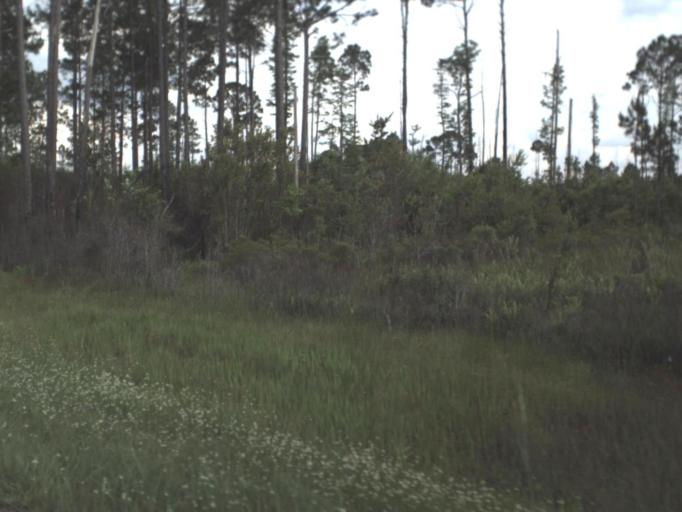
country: US
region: Florida
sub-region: Baker County
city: Macclenny
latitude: 30.5344
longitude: -82.3207
